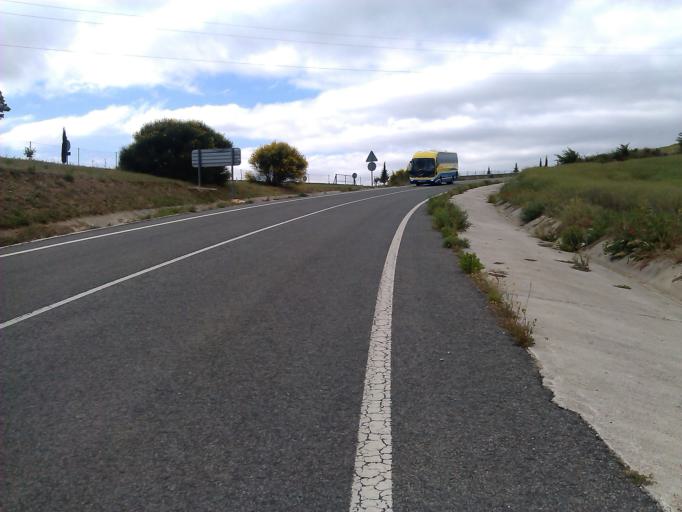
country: ES
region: Navarre
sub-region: Provincia de Navarra
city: Puente la Reina
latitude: 42.6700
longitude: -1.8302
